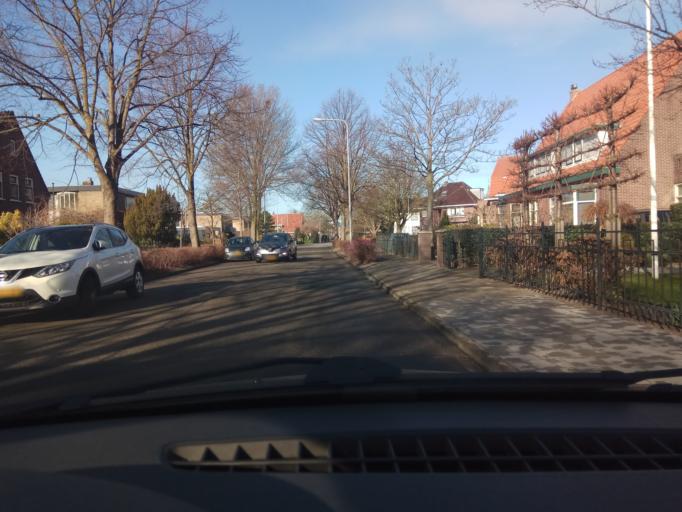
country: NL
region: South Holland
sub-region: Gemeente Westland
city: Naaldwijk
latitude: 51.9905
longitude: 4.2136
